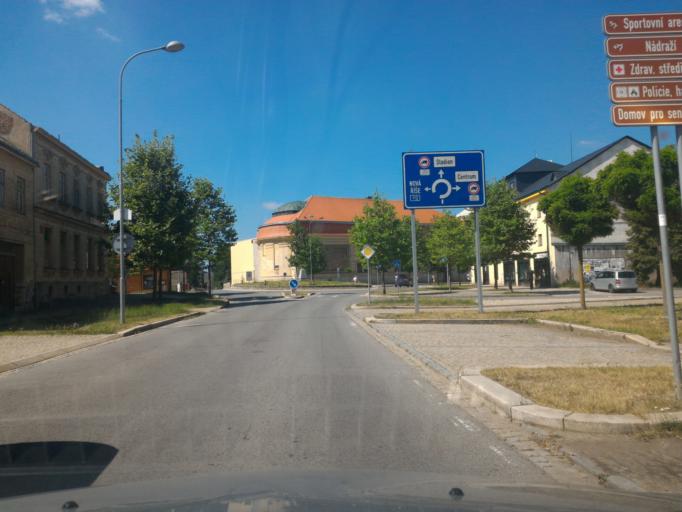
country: CZ
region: Vysocina
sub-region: Okres Jihlava
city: Telc
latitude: 49.1834
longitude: 15.4631
